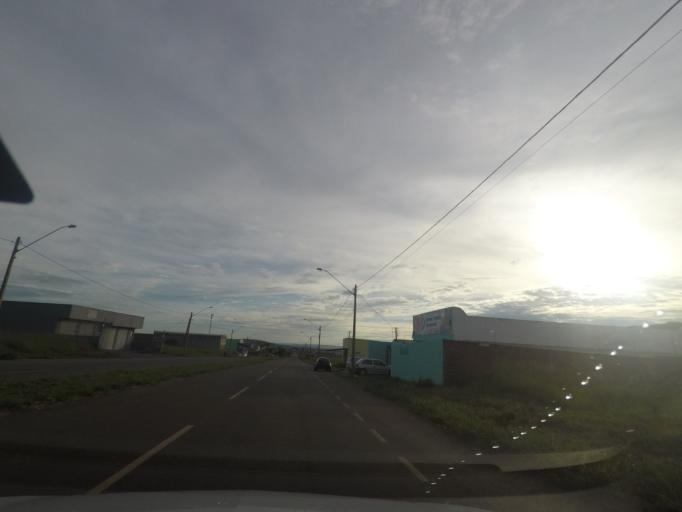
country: BR
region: Goias
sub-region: Trindade
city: Trindade
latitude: -16.7276
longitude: -49.4078
